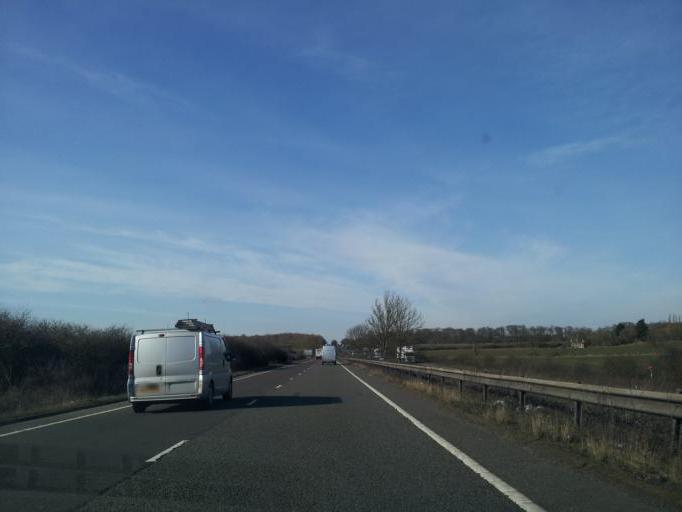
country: GB
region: England
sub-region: District of Rutland
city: Tickencote
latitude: 52.6849
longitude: -0.5509
